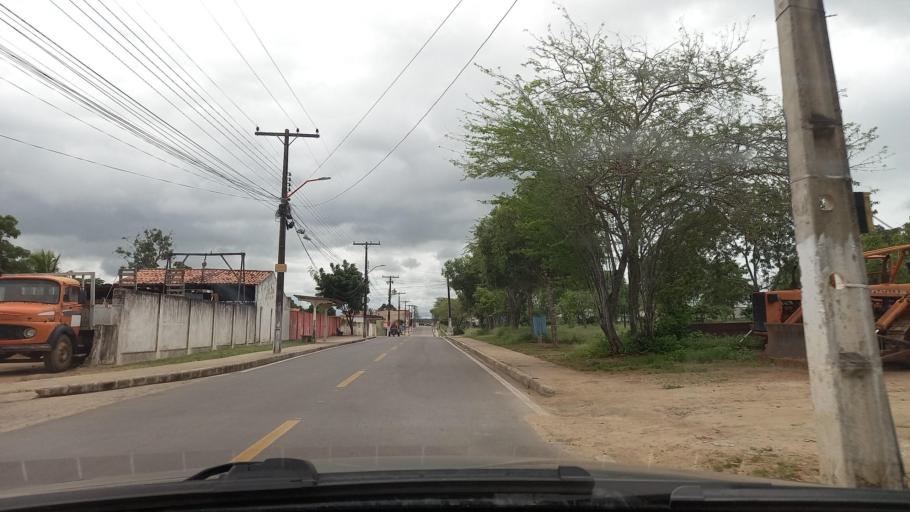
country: BR
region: Sergipe
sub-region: Caninde De Sao Francisco
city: Caninde de Sao Francisco
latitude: -9.6120
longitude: -37.7634
